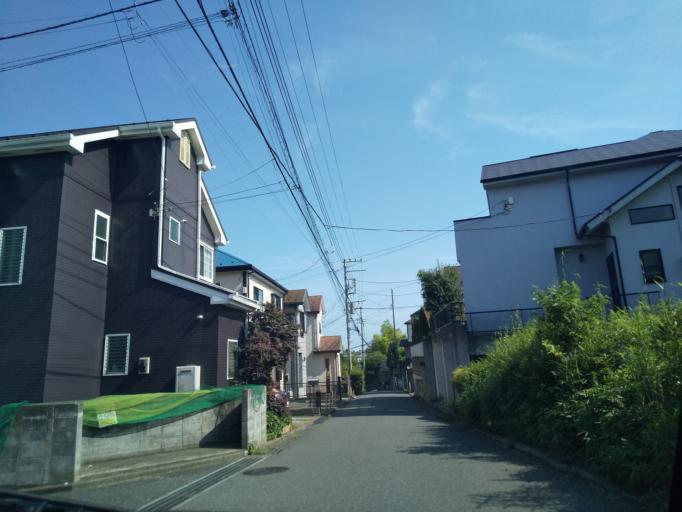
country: JP
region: Kanagawa
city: Minami-rinkan
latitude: 35.4611
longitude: 139.4186
